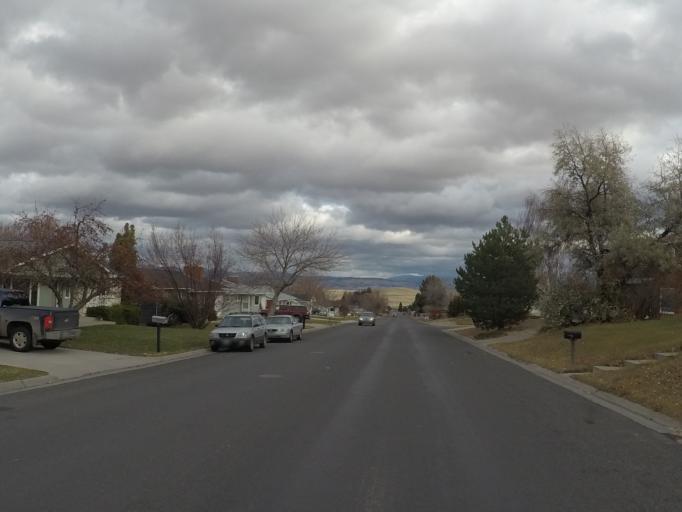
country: US
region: Montana
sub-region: Lewis and Clark County
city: Helena
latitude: 46.5814
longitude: -112.0047
